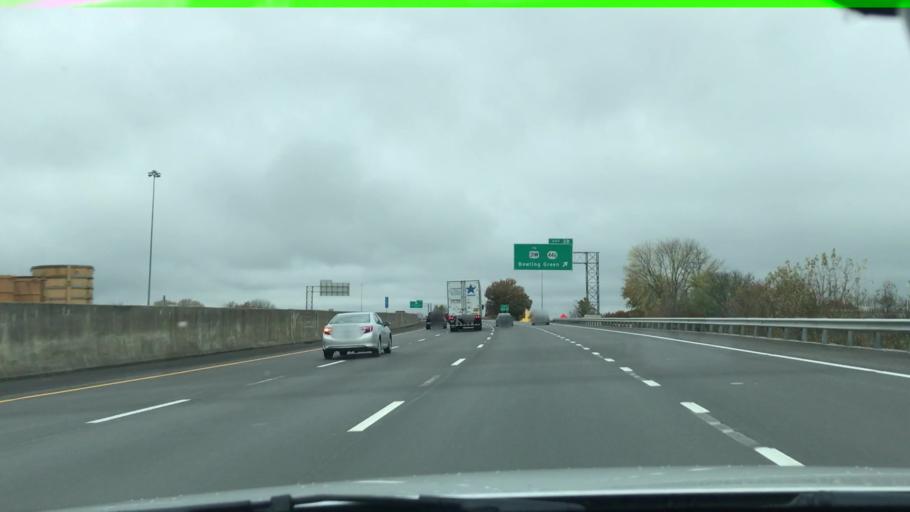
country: US
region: Kentucky
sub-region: Warren County
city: Bowling Green
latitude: 37.0073
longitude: -86.3655
